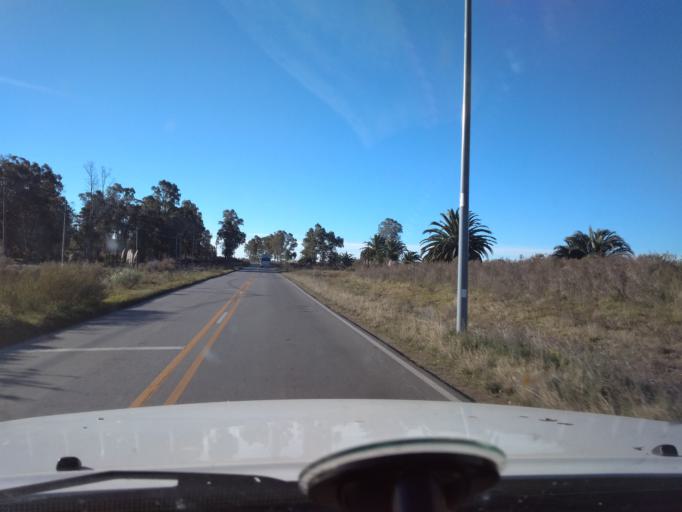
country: UY
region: Canelones
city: San Bautista
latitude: -34.4341
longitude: -55.9606
